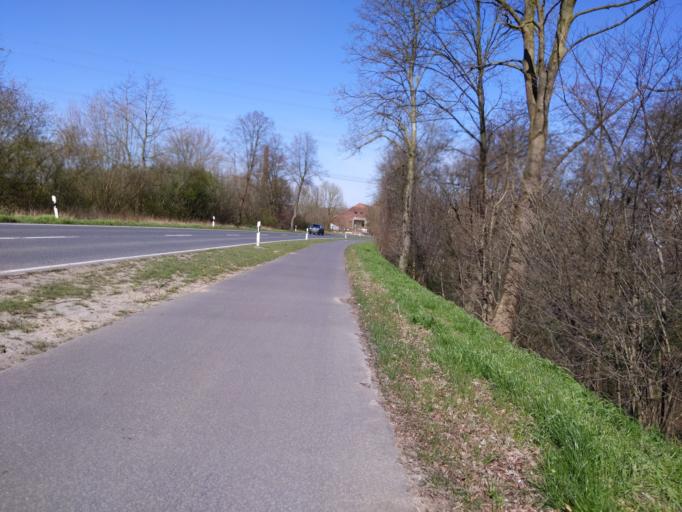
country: DE
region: North Rhine-Westphalia
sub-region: Regierungsbezirk Dusseldorf
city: Schermbeck
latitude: 51.6753
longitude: 6.8606
